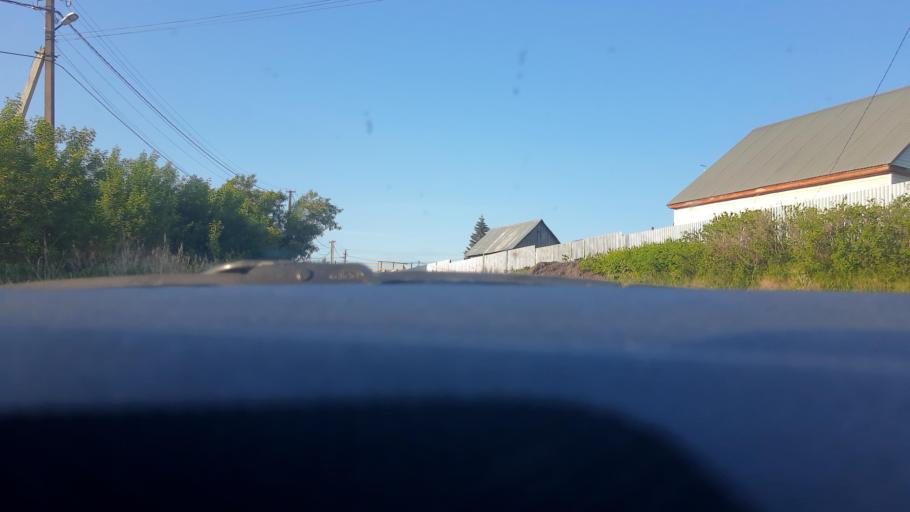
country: RU
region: Bashkortostan
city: Avdon
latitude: 54.6409
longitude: 55.5541
